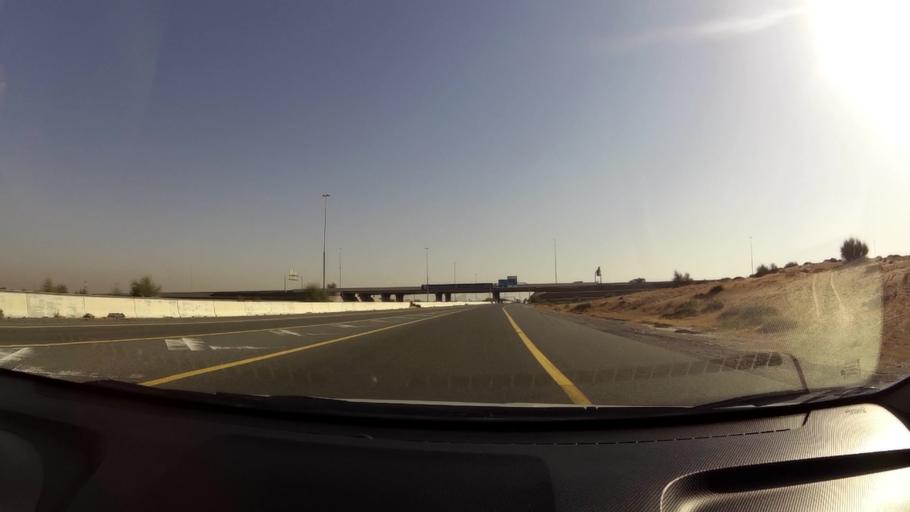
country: AE
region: Umm al Qaywayn
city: Umm al Qaywayn
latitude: 25.4536
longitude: 55.6159
